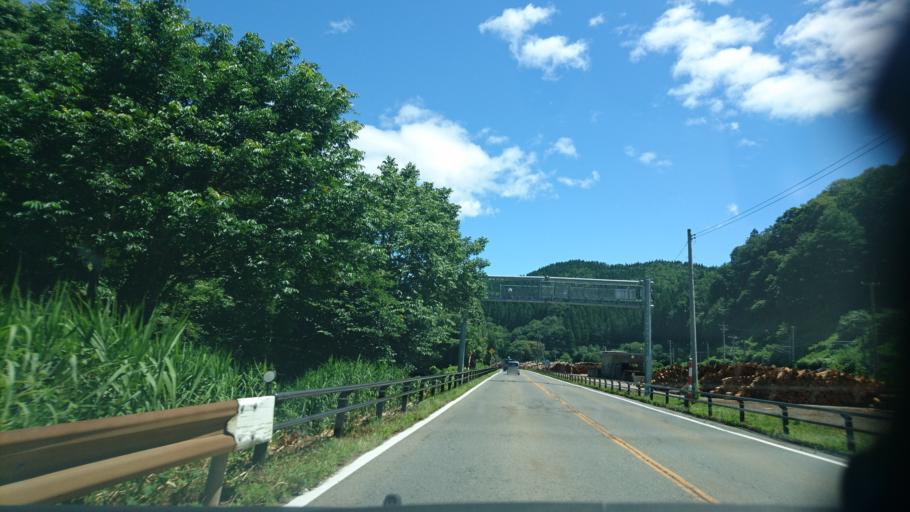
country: JP
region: Akita
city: Kakunodatemachi
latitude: 39.6521
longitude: 140.6697
